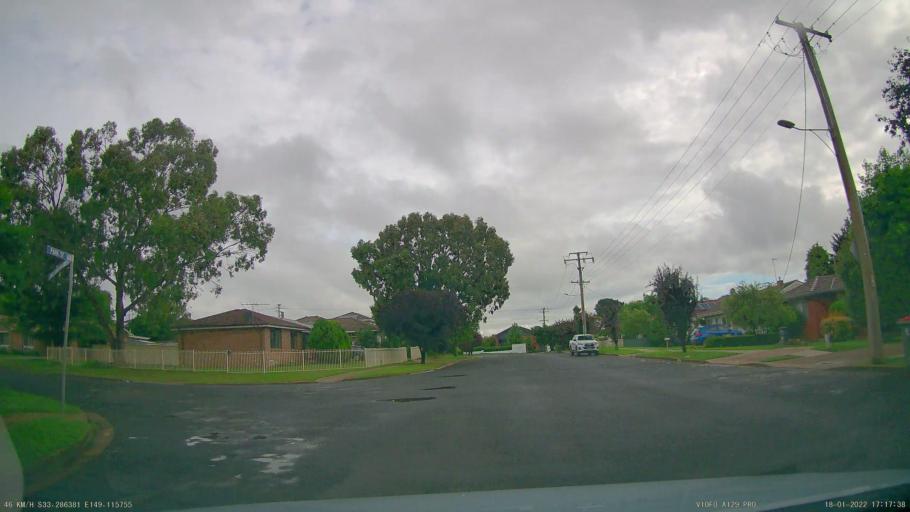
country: AU
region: New South Wales
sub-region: Orange Municipality
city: Orange
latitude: -33.2864
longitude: 149.1157
